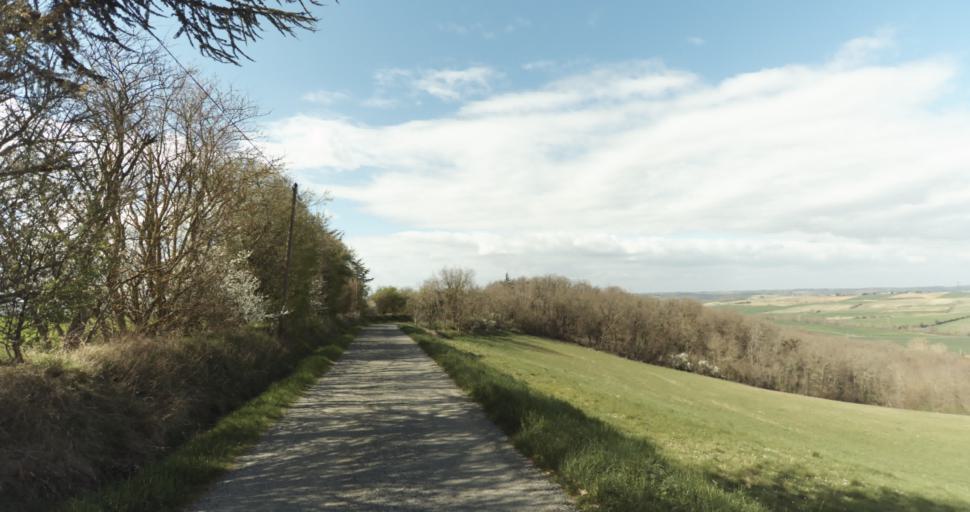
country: FR
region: Midi-Pyrenees
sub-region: Departement de la Haute-Garonne
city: Auterive
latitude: 43.3766
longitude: 1.5010
